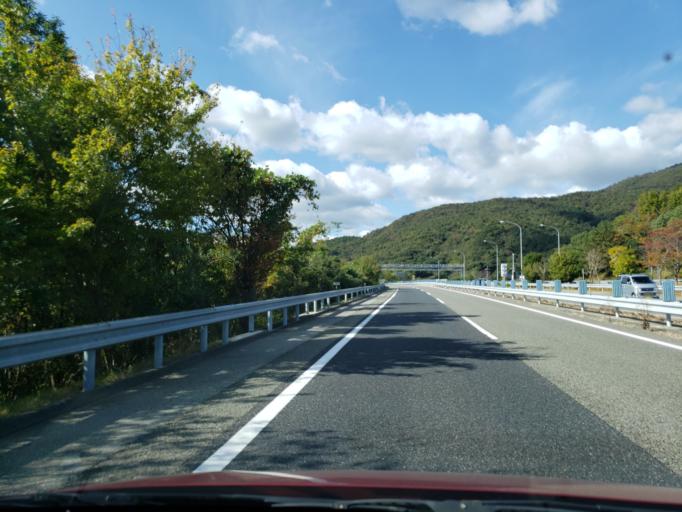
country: JP
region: Tokushima
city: Ishii
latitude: 34.1396
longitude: 134.4096
